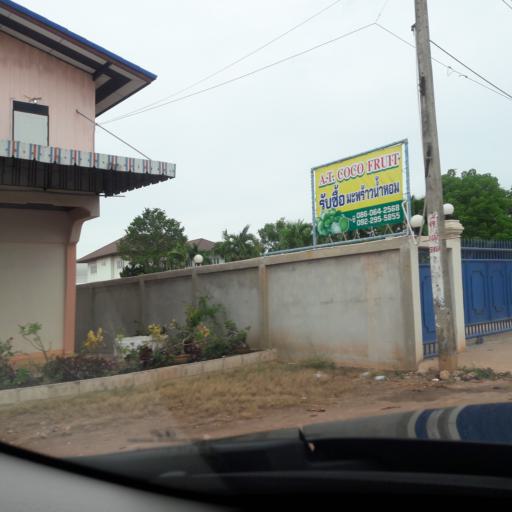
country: TH
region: Ratchaburi
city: Damnoen Saduak
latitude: 13.5586
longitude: 99.9617
